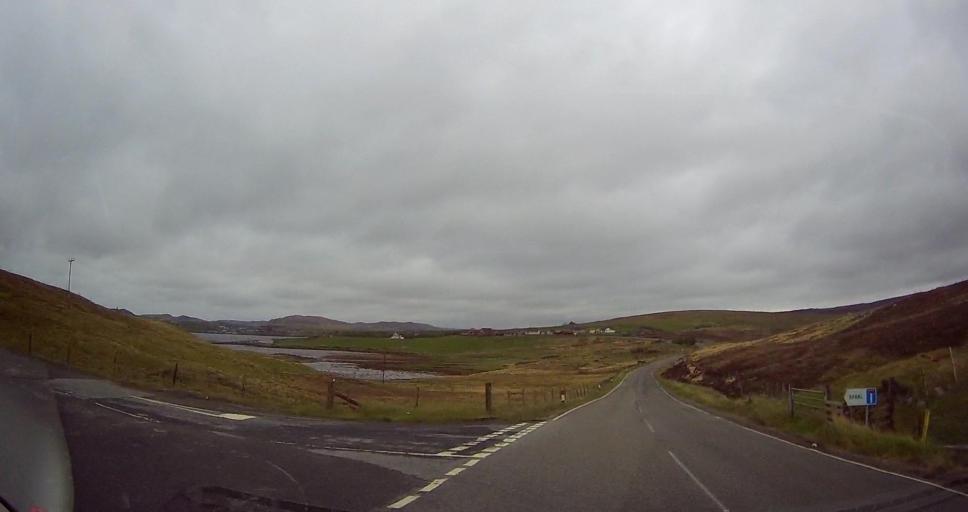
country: GB
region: Scotland
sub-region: Shetland Islands
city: Lerwick
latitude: 60.3801
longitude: -1.3423
